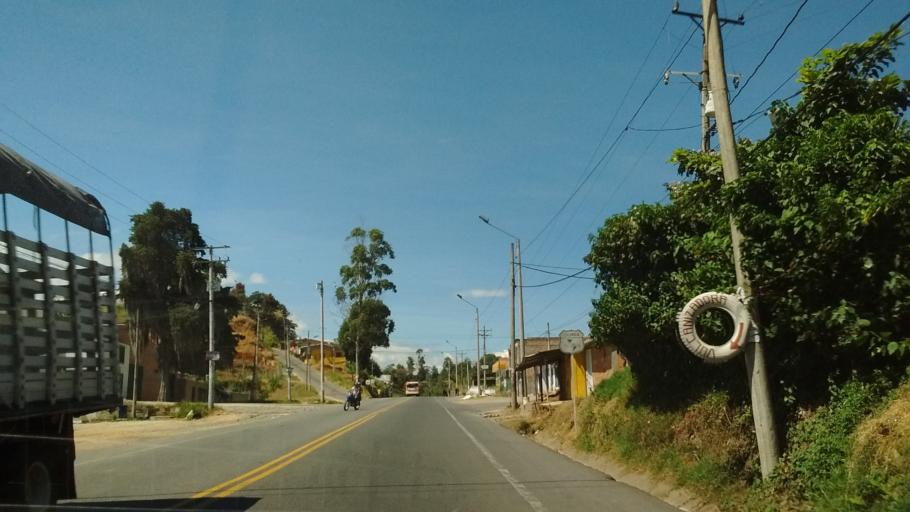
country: CO
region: Cauca
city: Popayan
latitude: 2.4284
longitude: -76.6213
